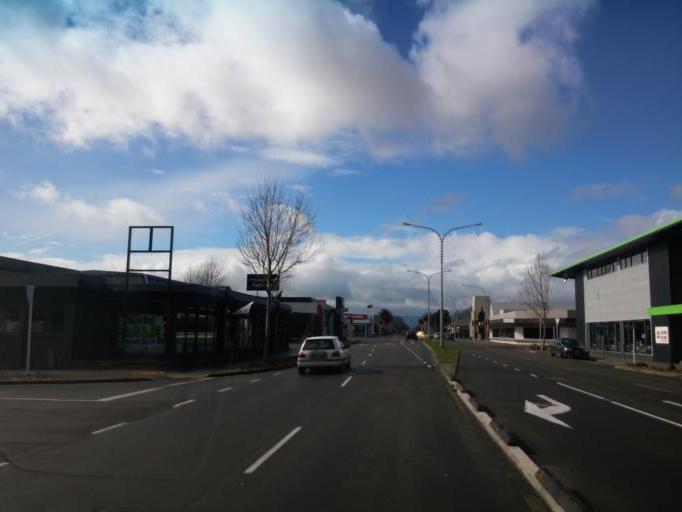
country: NZ
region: Manawatu-Wanganui
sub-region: Palmerston North City
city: Palmerston North
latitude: -40.3580
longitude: 175.6167
